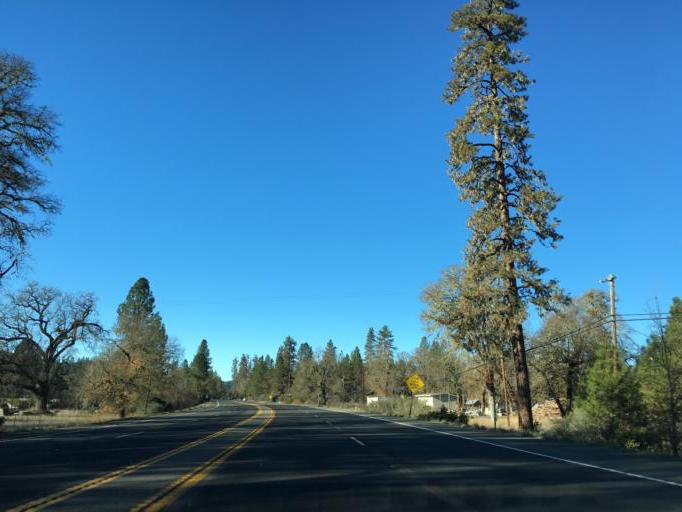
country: US
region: California
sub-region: Mendocino County
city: Laytonville
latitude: 39.7283
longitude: -123.5056
